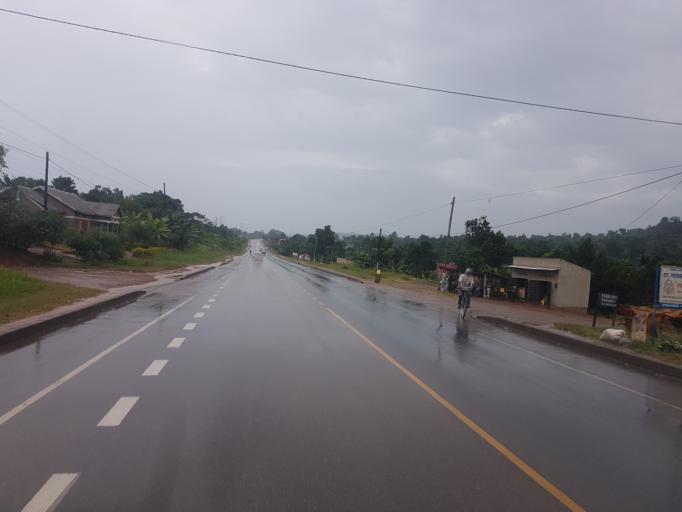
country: UG
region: Central Region
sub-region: Mpigi District
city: Mpigi
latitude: 0.1786
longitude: 32.2790
